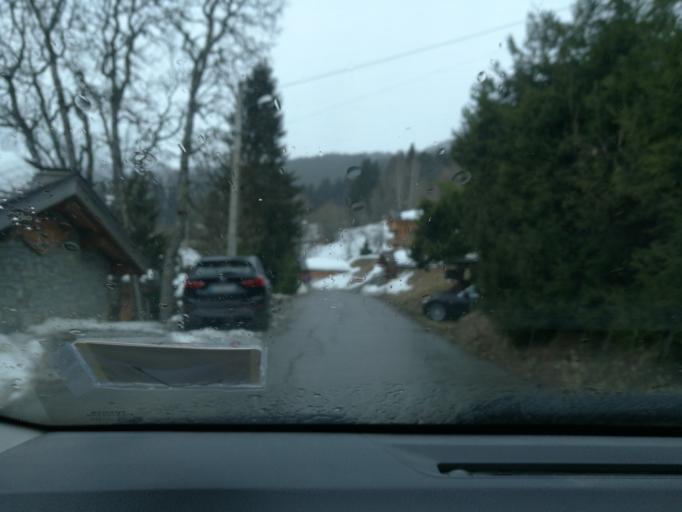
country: FR
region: Rhone-Alpes
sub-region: Departement de la Haute-Savoie
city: Saint-Gervais-les-Bains
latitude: 45.8709
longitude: 6.6896
